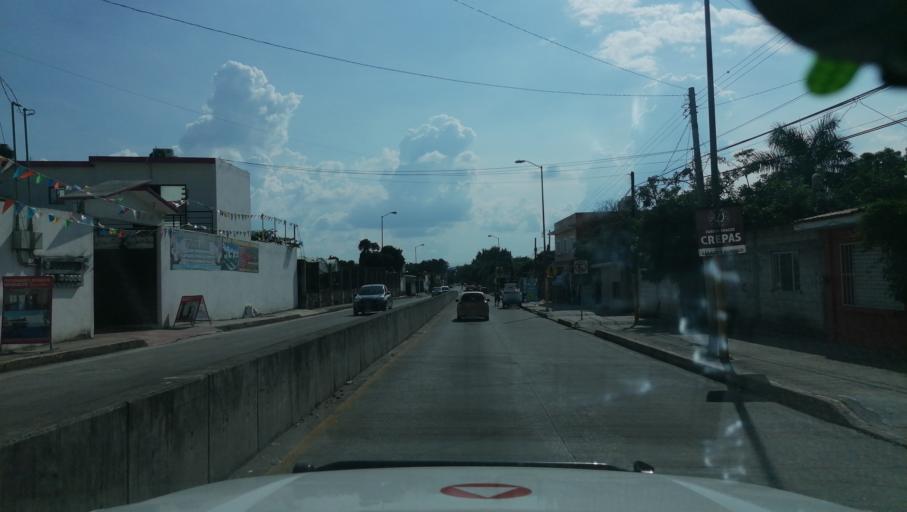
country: MX
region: Morelos
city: Cuautla Morelos
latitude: 18.8342
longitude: -98.9525
